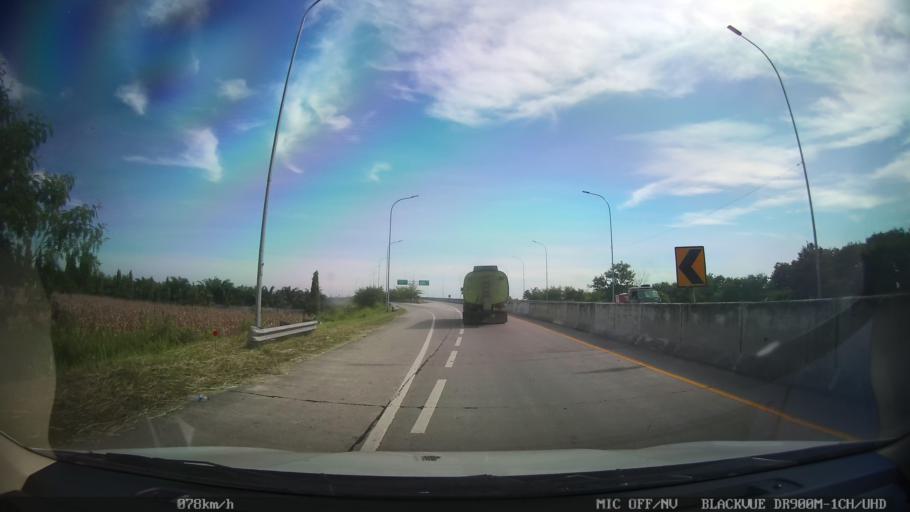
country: ID
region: North Sumatra
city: Medan
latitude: 3.6337
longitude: 98.6359
